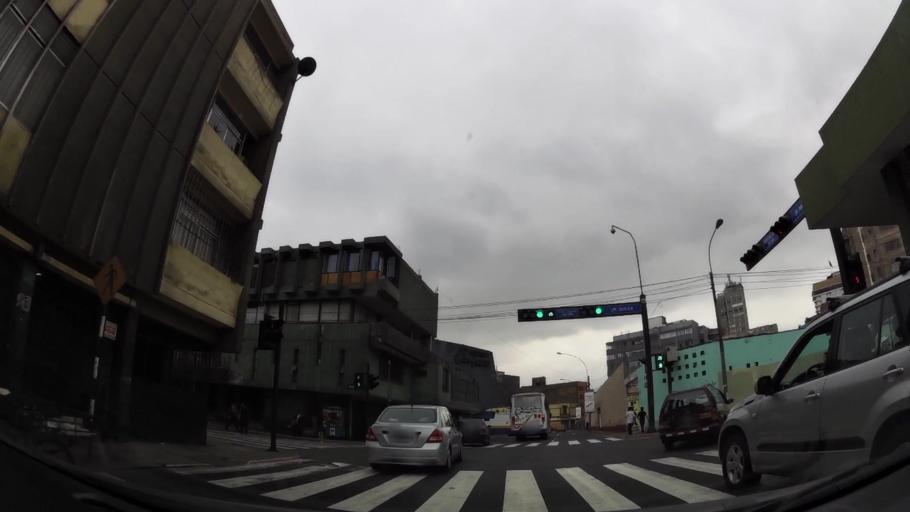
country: PE
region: Lima
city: Lima
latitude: -12.0511
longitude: -77.0399
